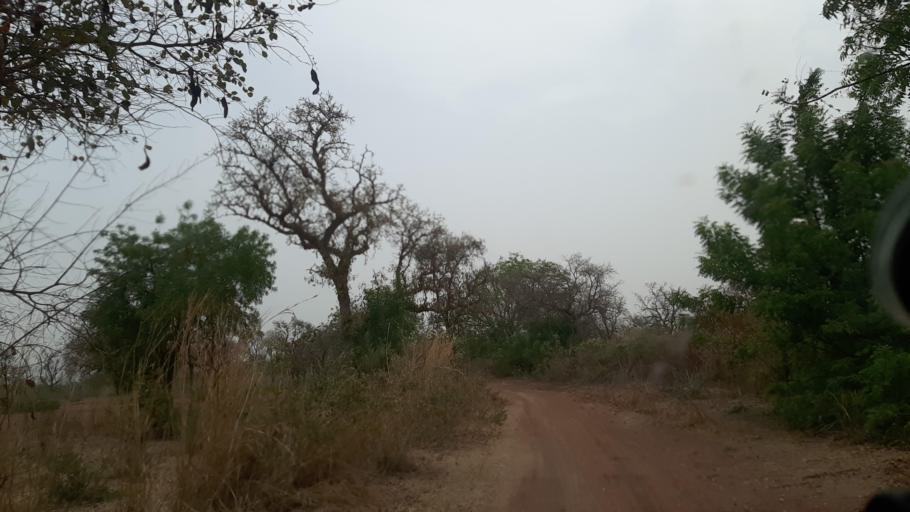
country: BF
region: Boucle du Mouhoun
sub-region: Province des Banwa
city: Salanso
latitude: 11.8484
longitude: -4.4213
